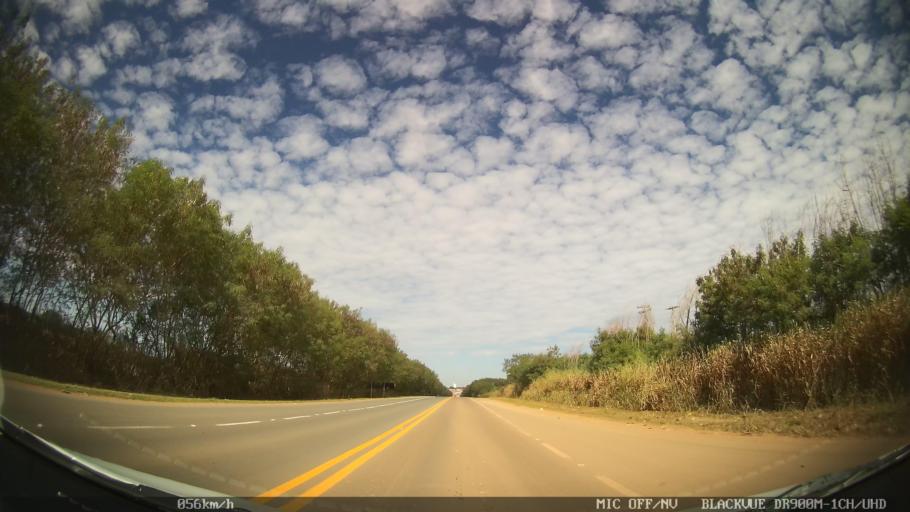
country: BR
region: Sao Paulo
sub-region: Santa Barbara D'Oeste
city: Santa Barbara d'Oeste
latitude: -22.7273
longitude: -47.4253
